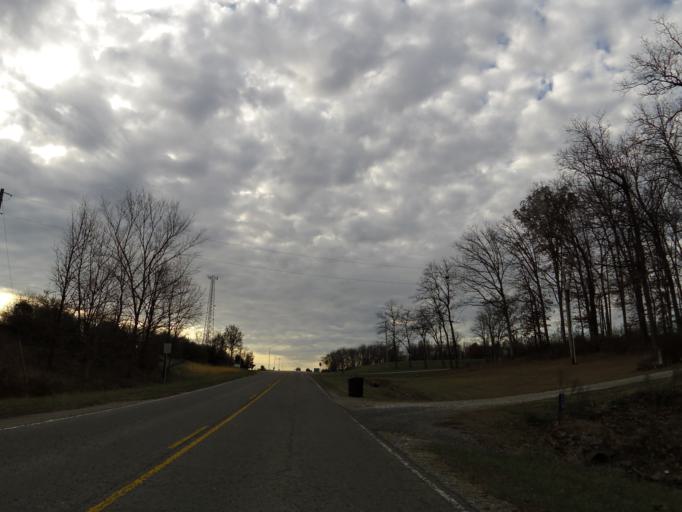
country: US
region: Illinois
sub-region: Jefferson County
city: Mount Vernon
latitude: 38.3678
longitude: -89.0348
